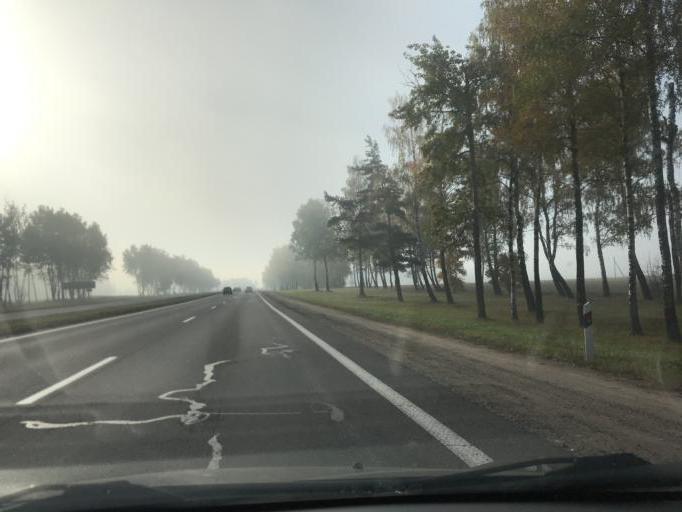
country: BY
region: Minsk
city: Luhavaya Slabada
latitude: 53.7832
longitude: 27.8231
